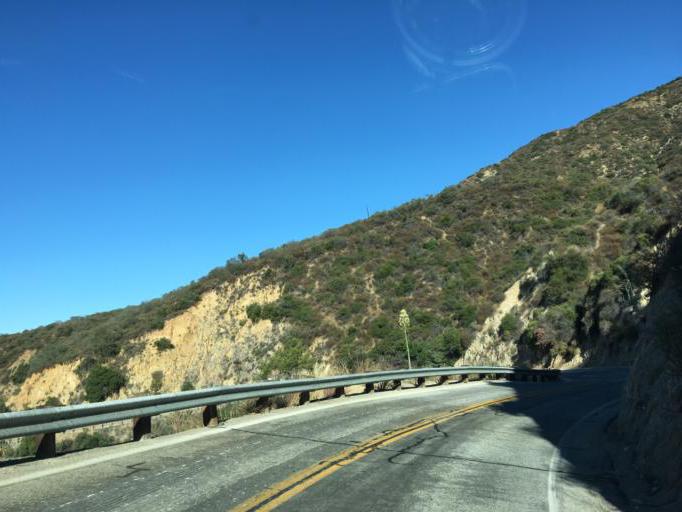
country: US
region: California
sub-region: Los Angeles County
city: Sierra Madre
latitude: 34.1773
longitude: -118.0280
